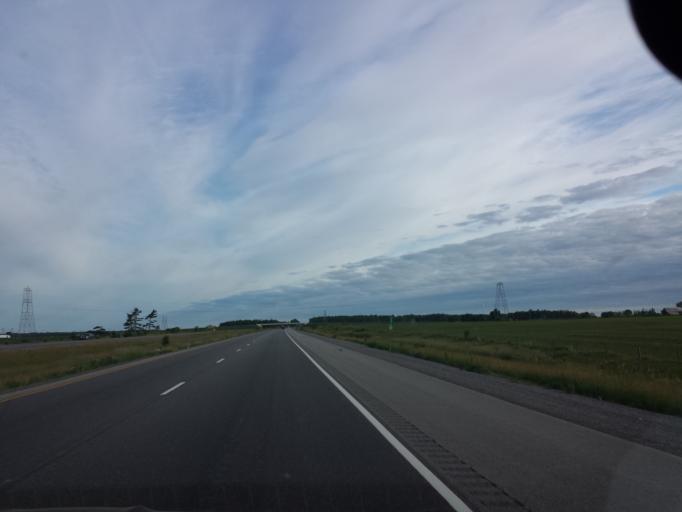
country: CA
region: Ontario
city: Arnprior
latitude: 45.3965
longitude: -76.2790
